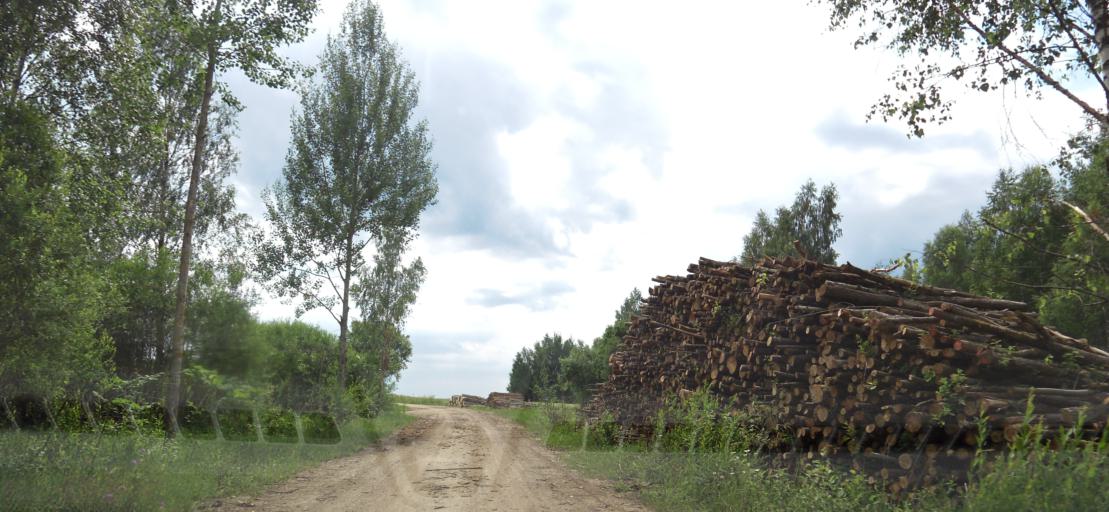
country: LV
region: Ogre
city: Jumprava
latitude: 56.4350
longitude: 24.9011
